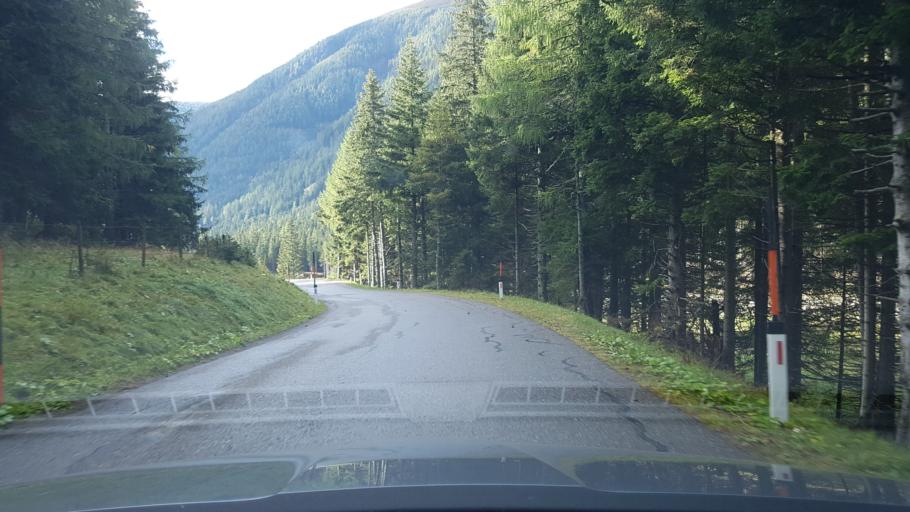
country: AT
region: Styria
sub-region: Politischer Bezirk Murau
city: Schoder
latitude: 47.2494
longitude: 14.0820
